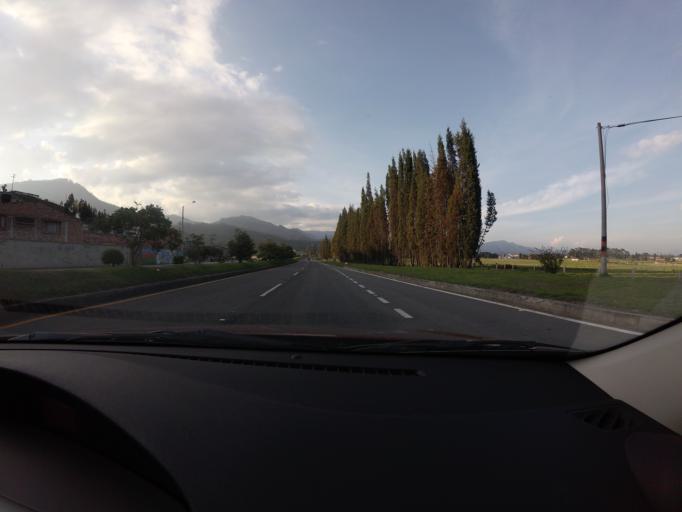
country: CO
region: Cundinamarca
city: Zipaquira
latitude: 5.0036
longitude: -74.0044
